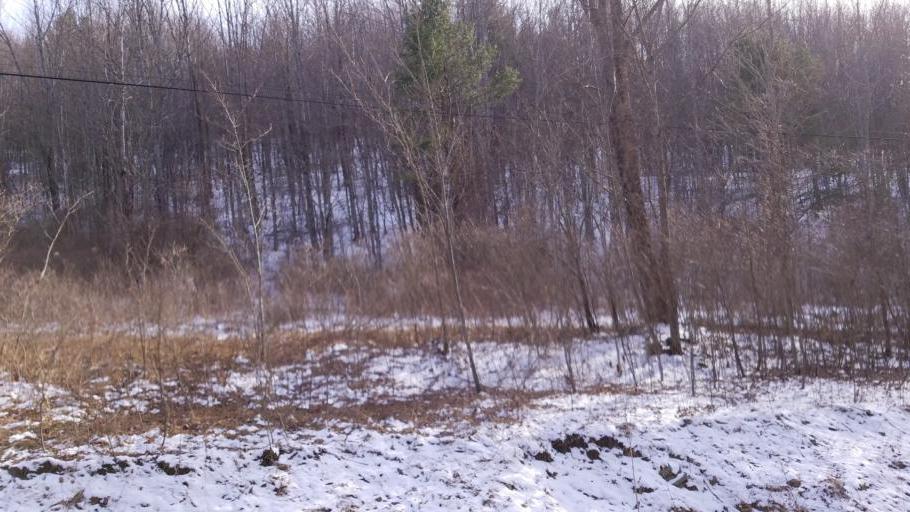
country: US
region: New York
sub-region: Allegany County
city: Wellsville
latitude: 42.1831
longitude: -77.8938
